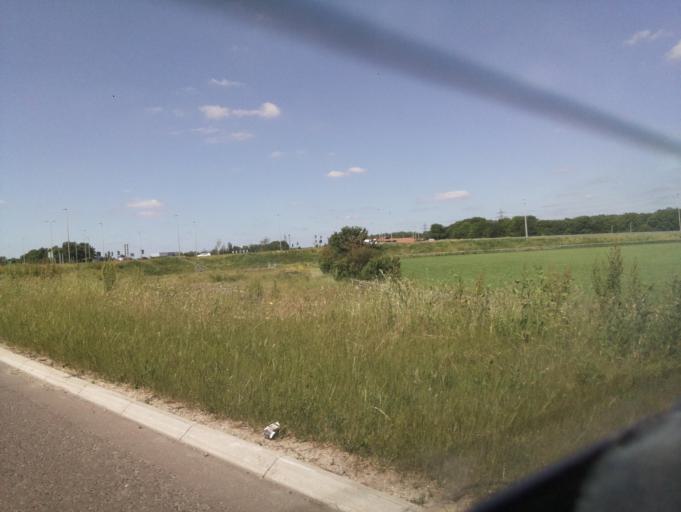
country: GB
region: England
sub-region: Wiltshire
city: Lydiard Tregoze
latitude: 51.5430
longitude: -1.8527
